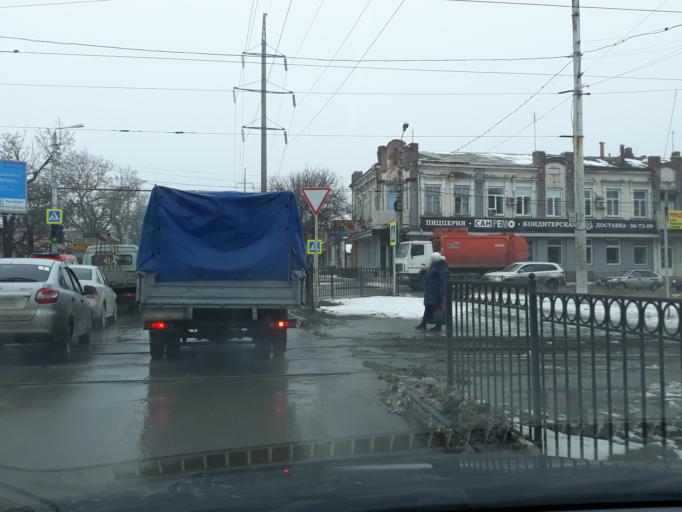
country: RU
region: Rostov
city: Taganrog
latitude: 47.2177
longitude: 38.9138
